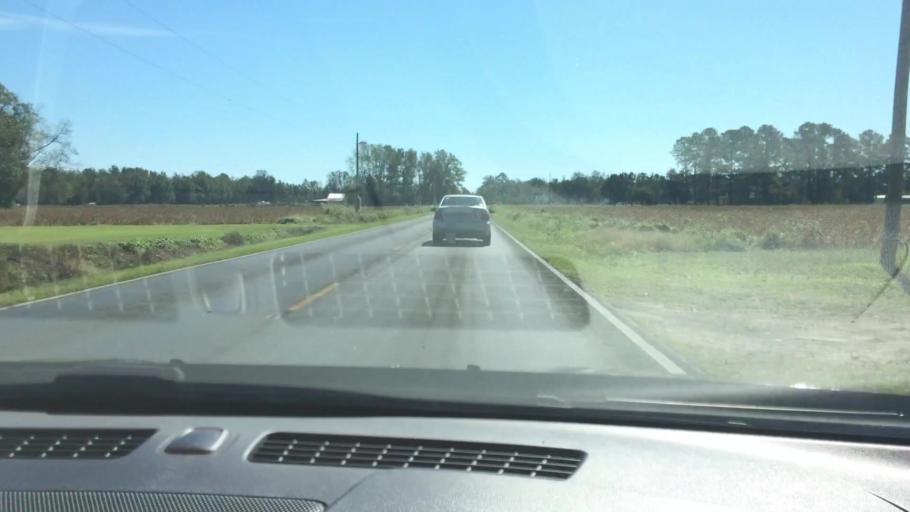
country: US
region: North Carolina
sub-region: Pitt County
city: Grifton
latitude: 35.3643
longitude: -77.3489
